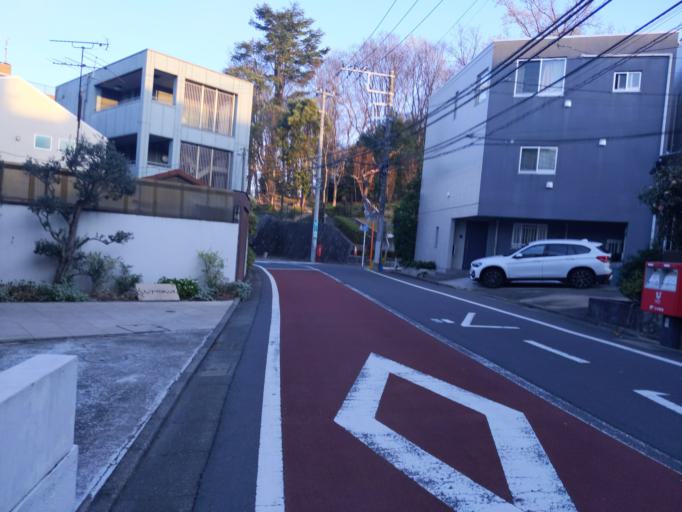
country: JP
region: Tokyo
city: Tokyo
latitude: 35.6271
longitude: 139.7055
